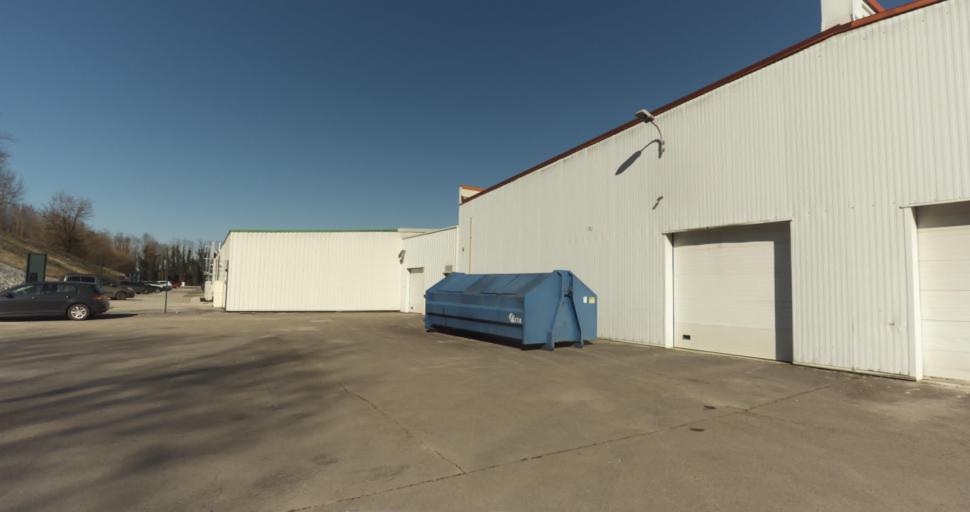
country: FR
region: Franche-Comte
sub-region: Departement du Jura
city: Montmorot
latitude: 46.6703
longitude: 5.5249
